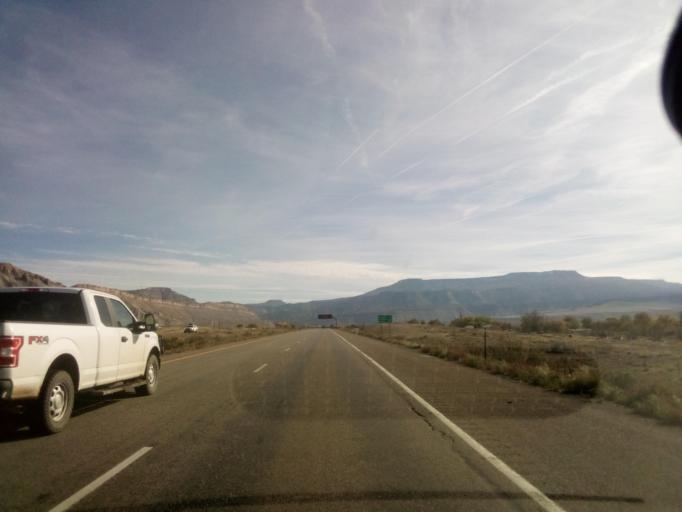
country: US
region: Colorado
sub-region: Mesa County
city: Clifton
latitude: 39.1079
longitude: -108.4358
